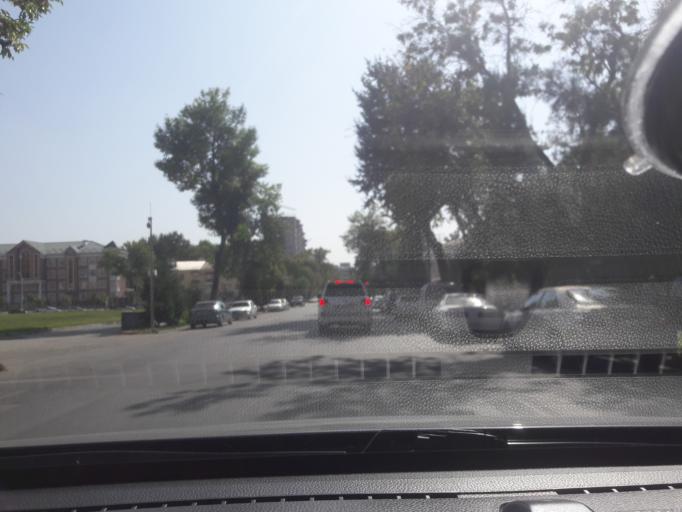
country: TJ
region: Dushanbe
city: Dushanbe
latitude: 38.5668
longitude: 68.7999
